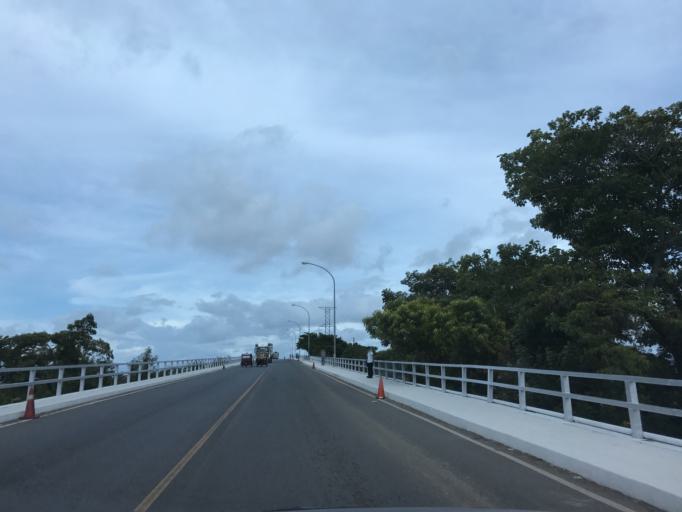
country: GT
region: Izabal
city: Morales
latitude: 15.6584
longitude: -89.0014
